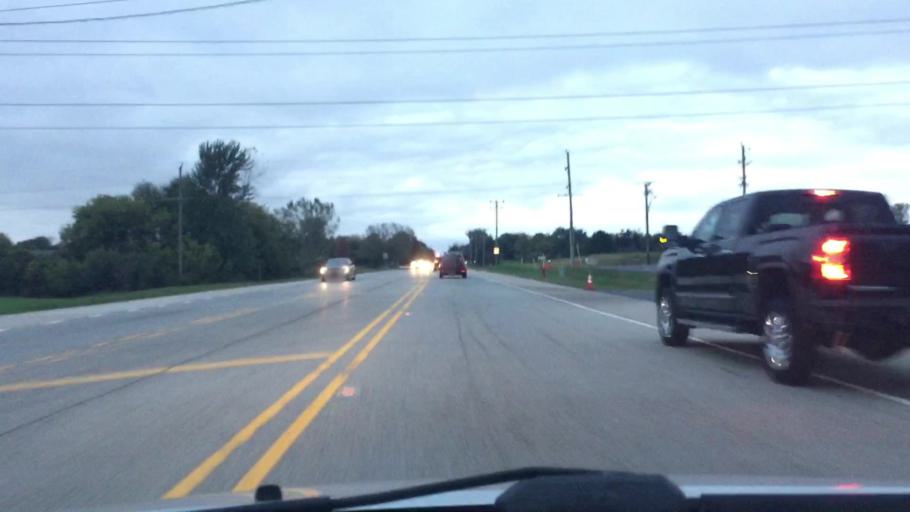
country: US
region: Illinois
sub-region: McHenry County
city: Crystal Lake
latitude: 42.2551
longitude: -88.2867
